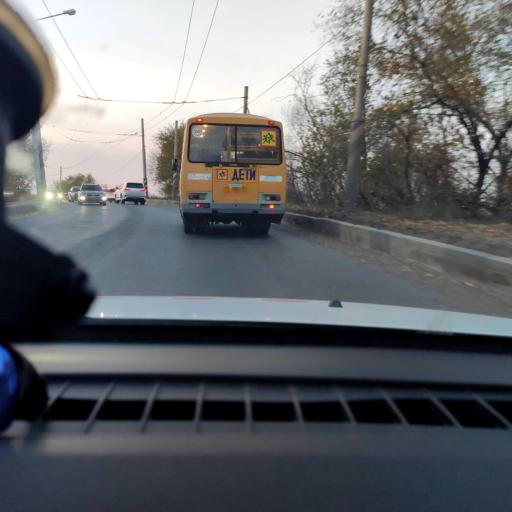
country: RU
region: Samara
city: Samara
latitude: 53.1502
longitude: 50.0939
